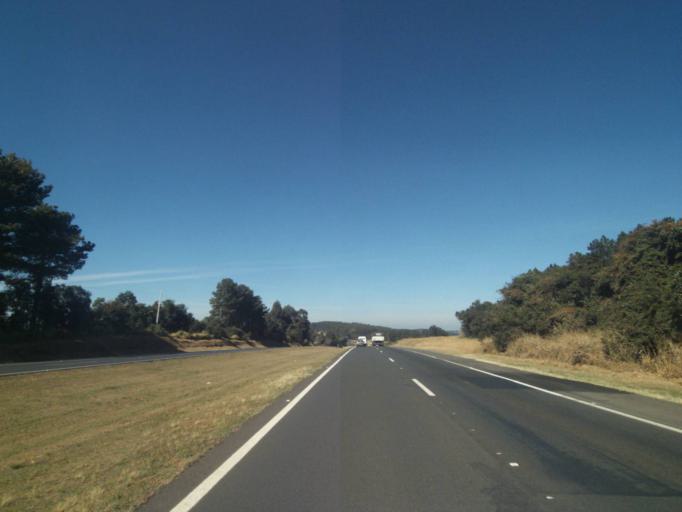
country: BR
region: Parana
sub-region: Carambei
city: Carambei
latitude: -24.8841
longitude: -50.4379
